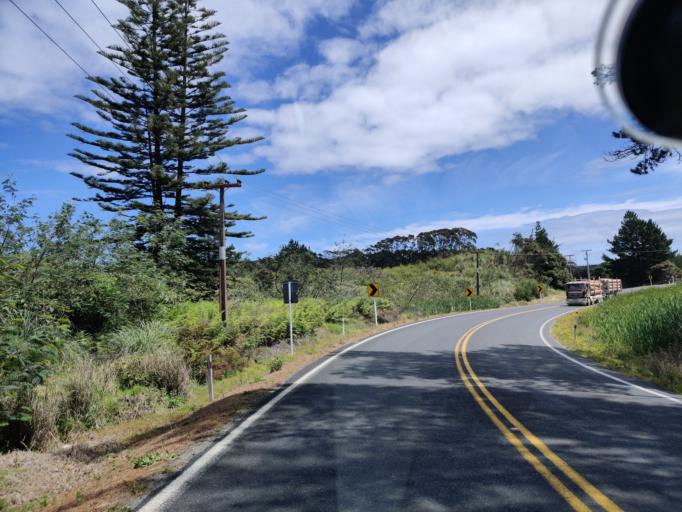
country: NZ
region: Northland
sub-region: Far North District
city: Kaitaia
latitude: -35.0062
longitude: 173.1952
